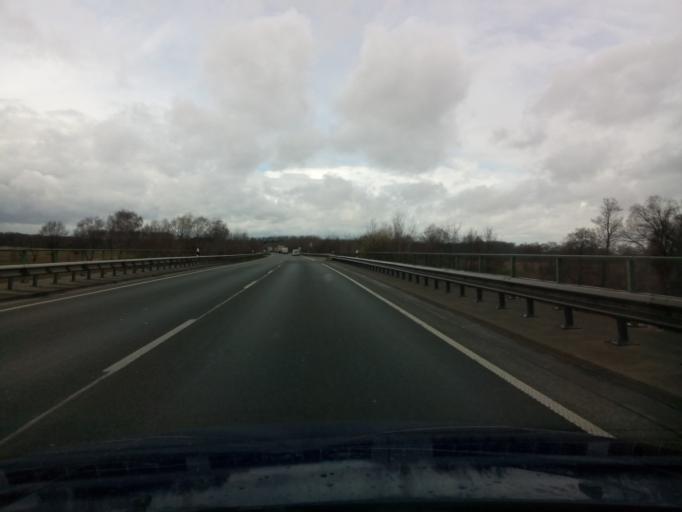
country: DE
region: Lower Saxony
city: Meppen
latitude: 52.7255
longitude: 7.2568
